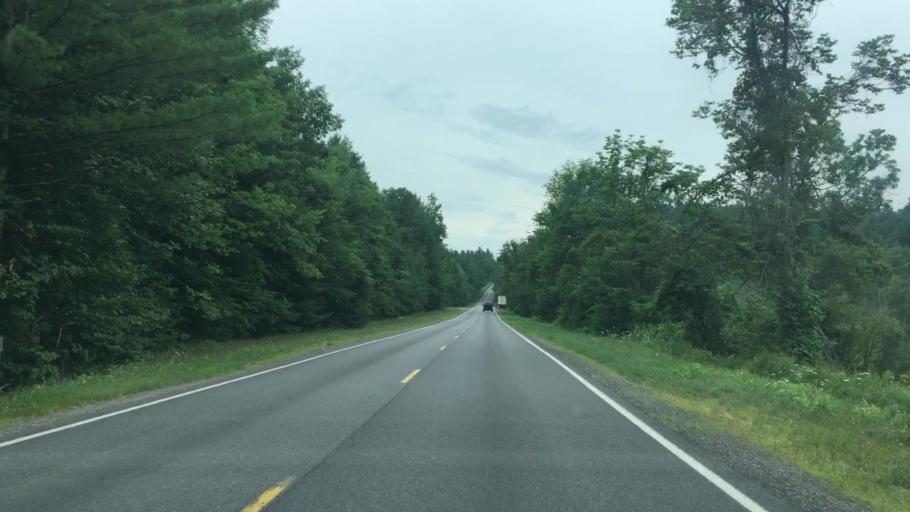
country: US
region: New York
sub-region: Clinton County
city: Peru
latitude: 44.4969
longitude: -73.5916
